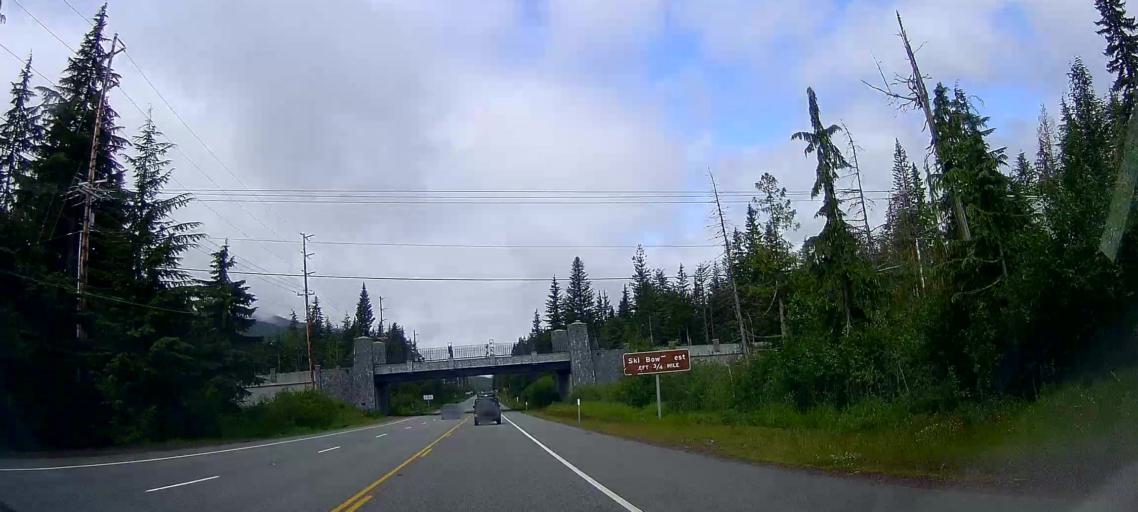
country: US
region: Oregon
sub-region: Clackamas County
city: Mount Hood Village
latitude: 45.3023
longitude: -121.7541
